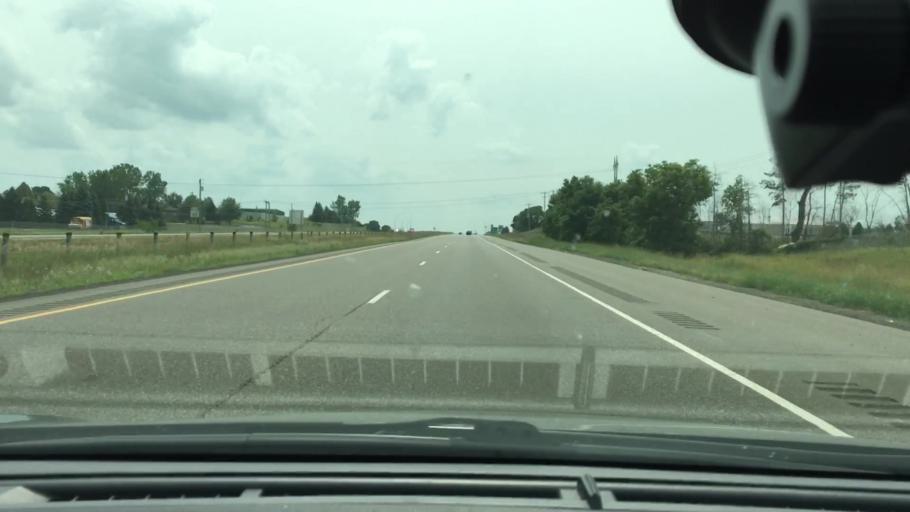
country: US
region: Minnesota
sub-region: Hennepin County
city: Rogers
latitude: 45.2198
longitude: -93.5527
